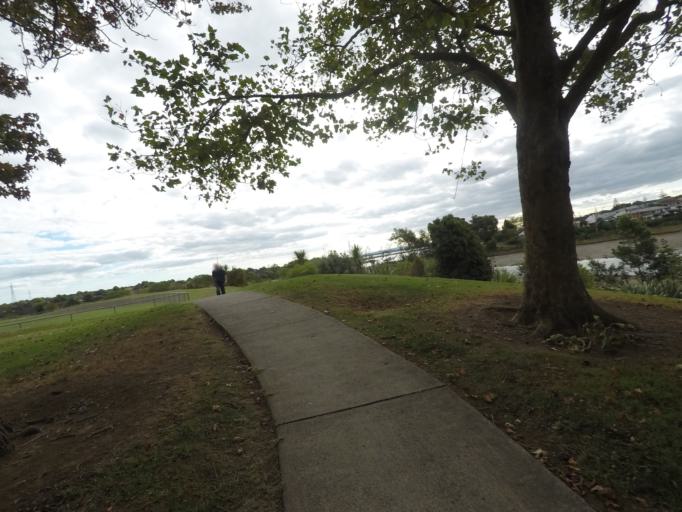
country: NZ
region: Auckland
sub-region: Auckland
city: Papakura
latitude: -37.0616
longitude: 174.9348
